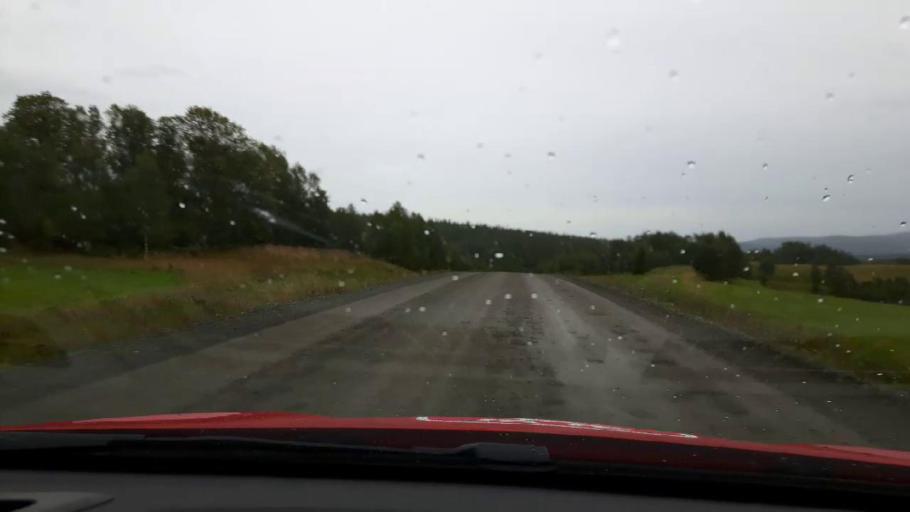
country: NO
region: Nord-Trondelag
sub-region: Meraker
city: Meraker
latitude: 63.5788
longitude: 12.2730
